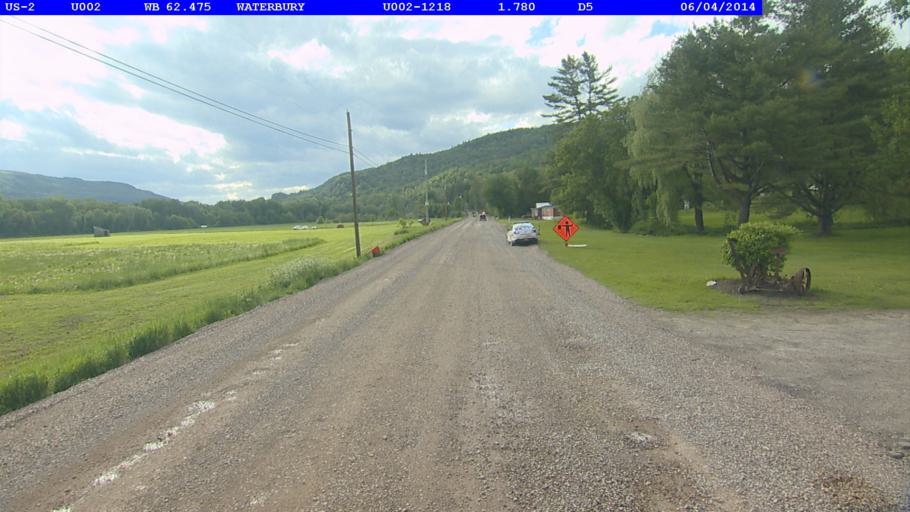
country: US
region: Vermont
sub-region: Washington County
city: Waterbury
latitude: 44.3564
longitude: -72.7927
